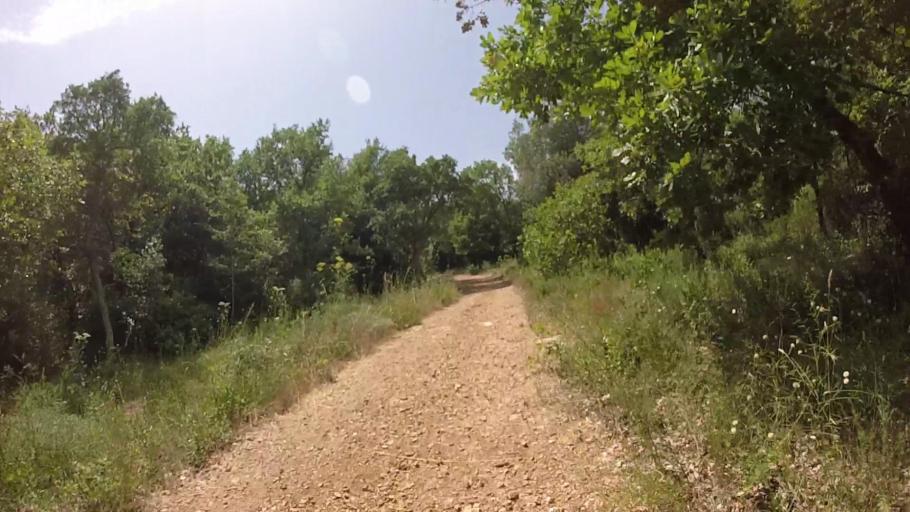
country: FR
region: Provence-Alpes-Cote d'Azur
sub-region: Departement des Alpes-Maritimes
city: Mougins
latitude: 43.6163
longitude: 7.0310
